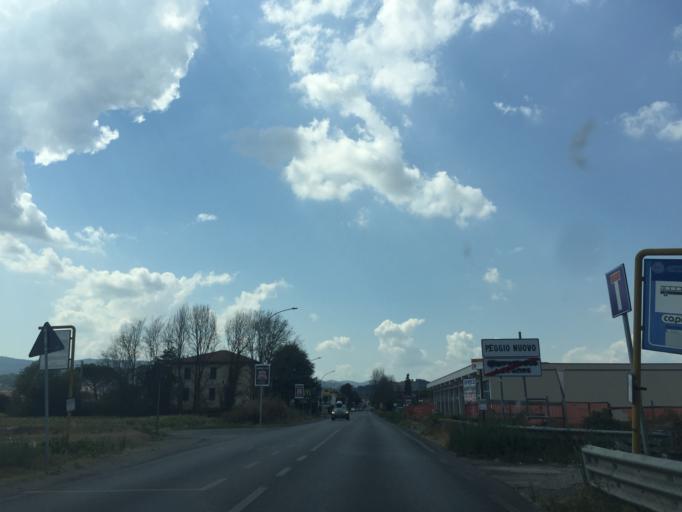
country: IT
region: Tuscany
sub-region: Provincia di Prato
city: Poggio A Caiano
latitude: 43.8132
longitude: 11.0684
